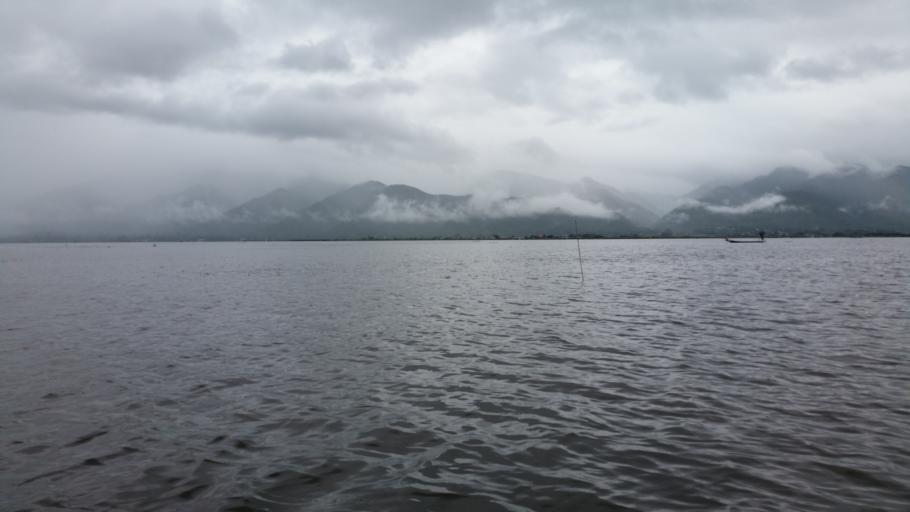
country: MM
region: Shan
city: Taunggyi
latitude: 20.5306
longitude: 96.9004
